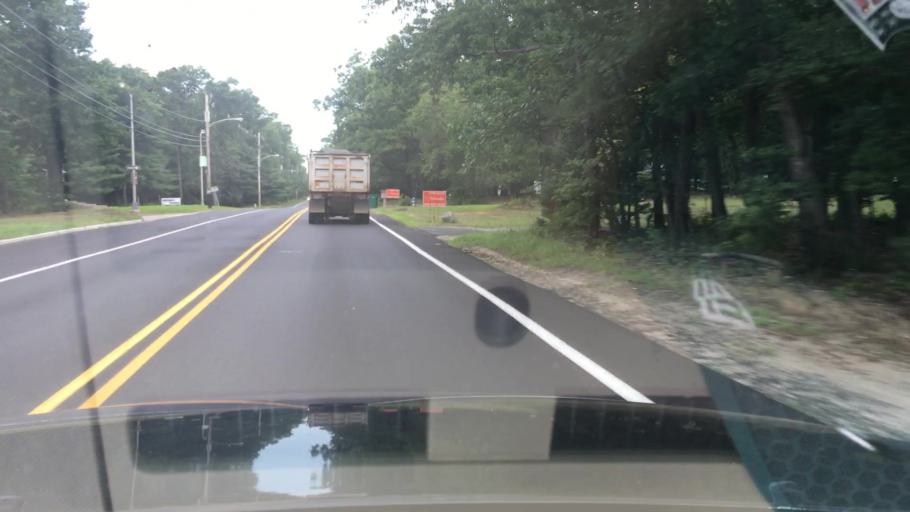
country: US
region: New Jersey
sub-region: Ocean County
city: Lakehurst
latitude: 40.0583
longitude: -74.3525
